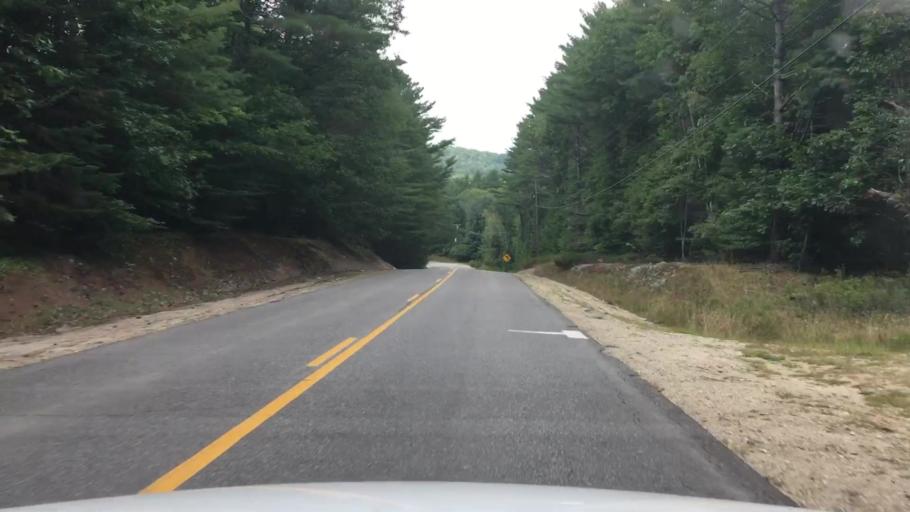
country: US
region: Maine
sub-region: Oxford County
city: Rumford
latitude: 44.5454
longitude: -70.6791
